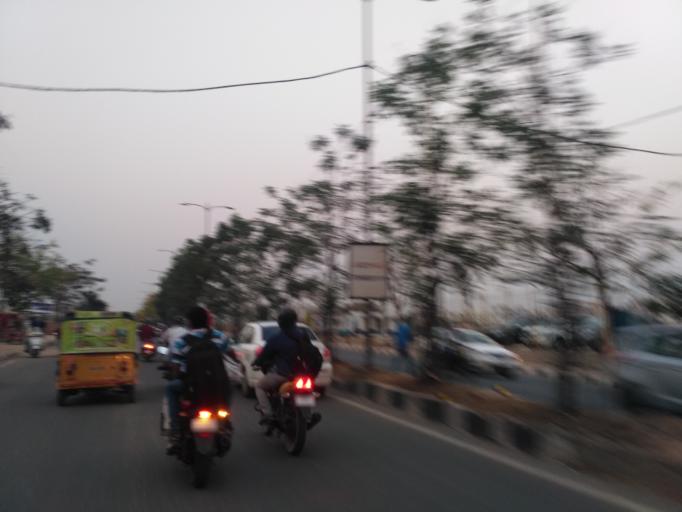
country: IN
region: Telangana
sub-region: Rangareddi
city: Kukatpalli
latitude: 17.4437
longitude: 78.3937
